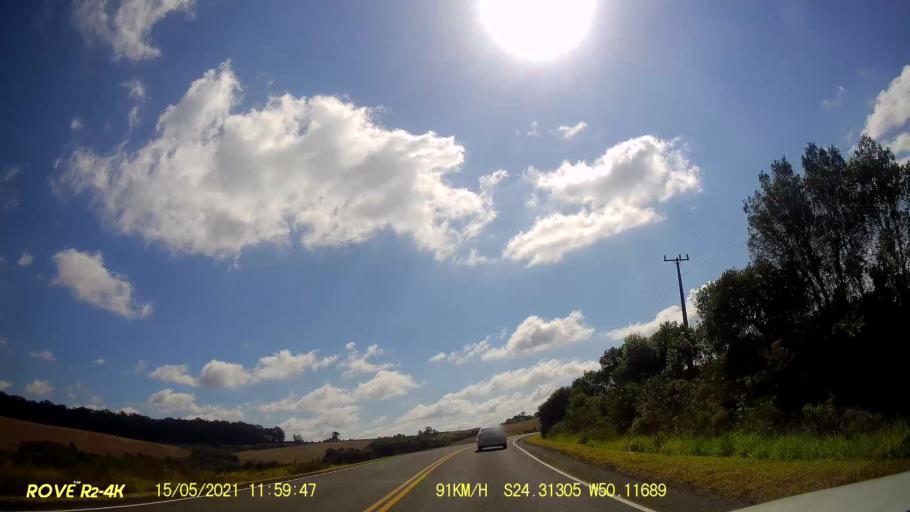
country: BR
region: Parana
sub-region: Pirai Do Sul
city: Pirai do Sul
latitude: -24.3132
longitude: -50.1168
